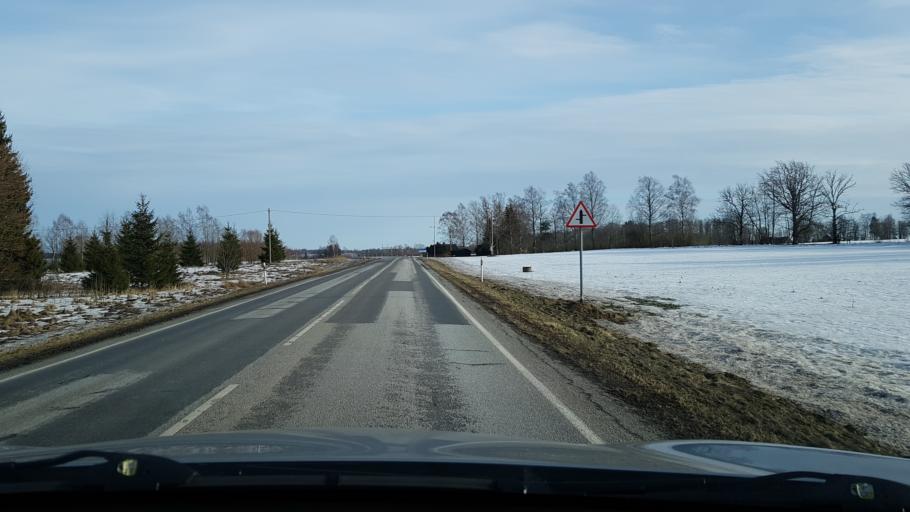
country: EE
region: Viljandimaa
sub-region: Viljandi linn
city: Viljandi
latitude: 58.3551
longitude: 25.4373
